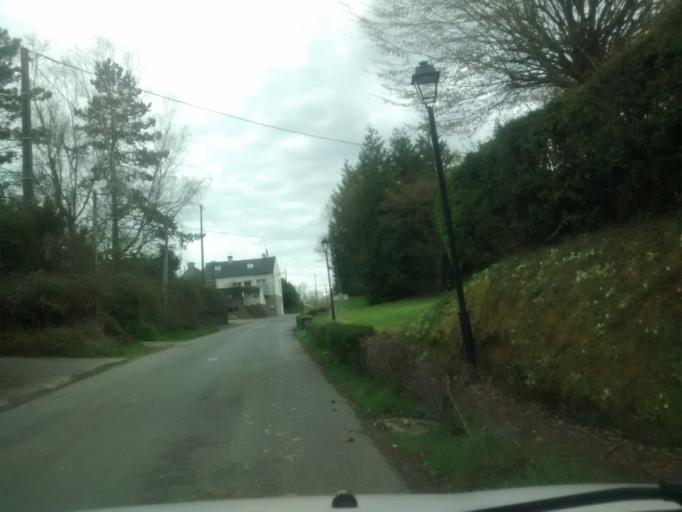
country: FR
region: Brittany
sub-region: Departement d'Ille-et-Vilaine
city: Saint-Sulpice-la-Foret
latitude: 48.2239
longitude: -1.5735
